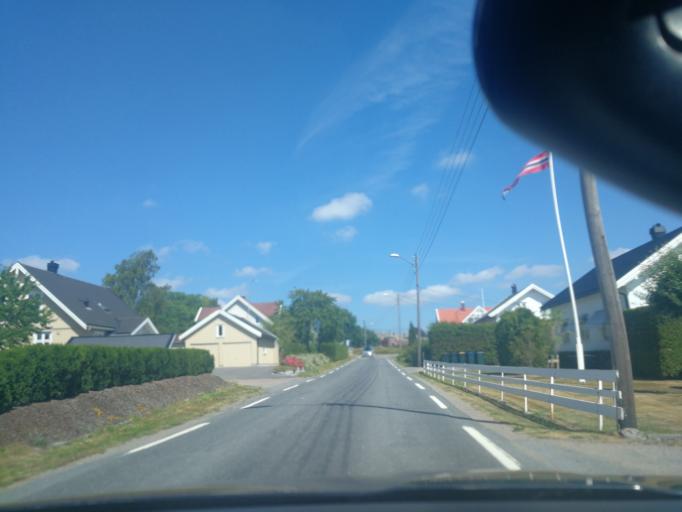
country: NO
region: Vestfold
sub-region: Stokke
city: Stokke
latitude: 59.2191
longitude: 10.2982
